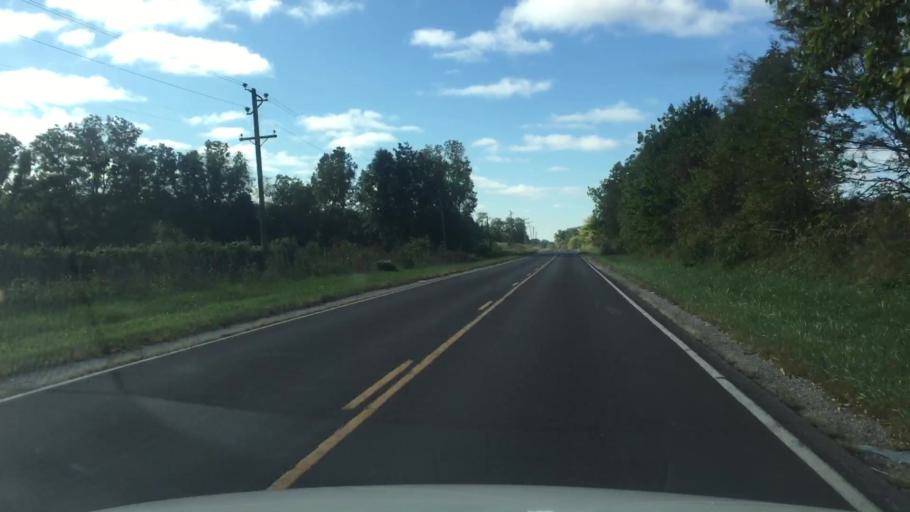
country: US
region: Missouri
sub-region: Howard County
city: New Franklin
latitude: 39.0554
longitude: -92.7443
